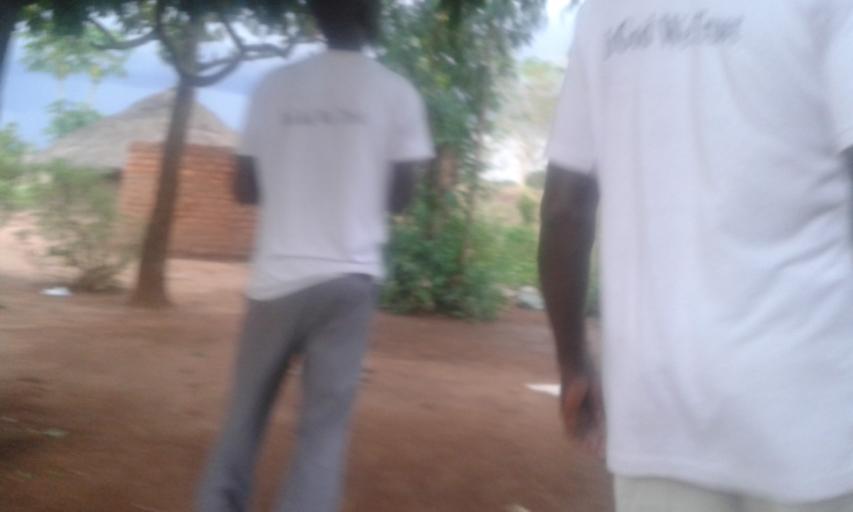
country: UG
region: Northern Region
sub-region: Gulu District
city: Gulu
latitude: 2.7942
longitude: 32.3228
